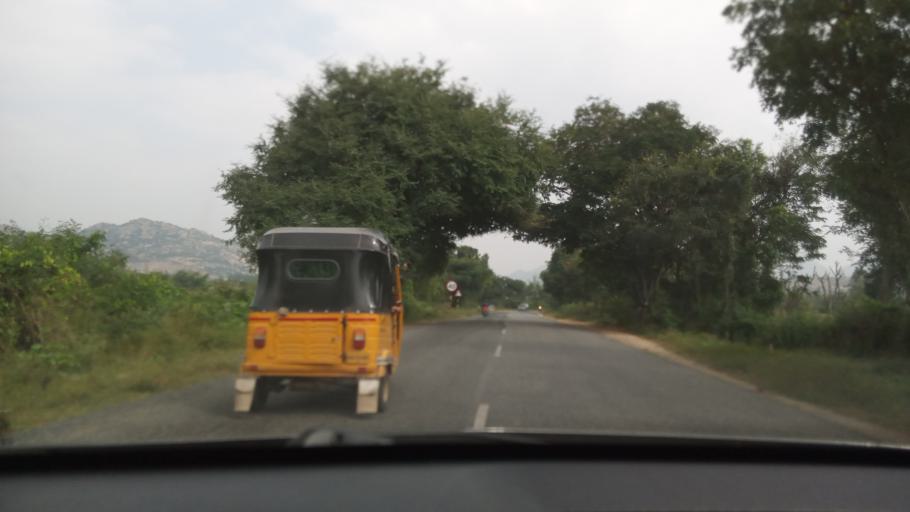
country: IN
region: Andhra Pradesh
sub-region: Chittoor
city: Pakala
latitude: 13.6563
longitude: 78.8382
